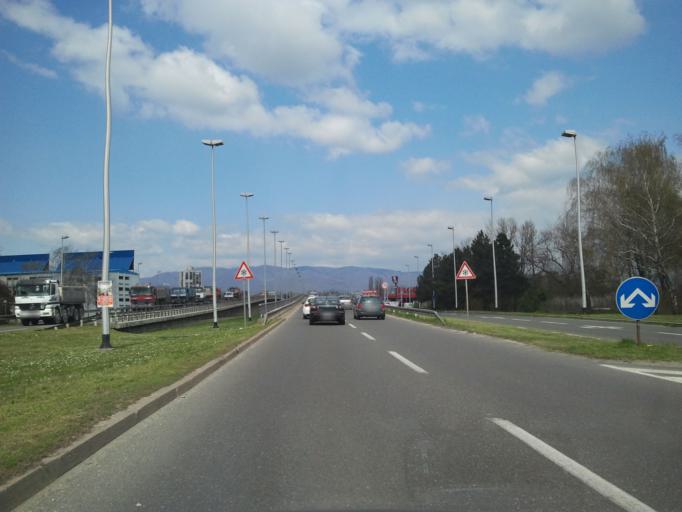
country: HR
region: Grad Zagreb
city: Novi Zagreb
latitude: 45.7747
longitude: 16.0034
